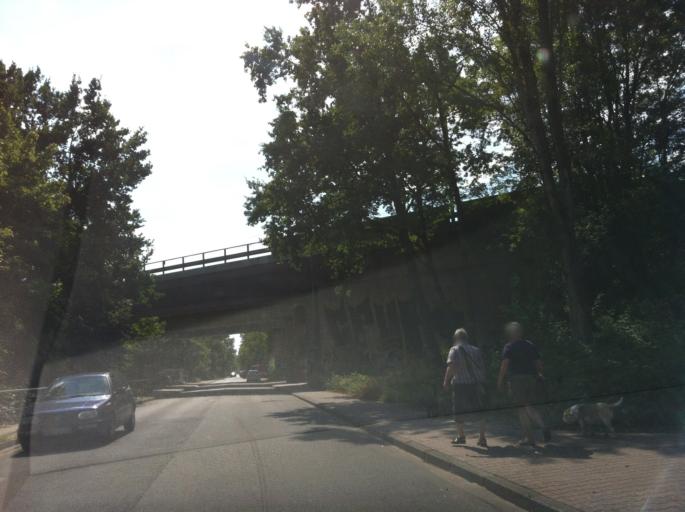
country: DE
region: Hesse
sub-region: Regierungsbezirk Darmstadt
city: Frankfurt am Main
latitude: 50.1438
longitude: 8.6431
